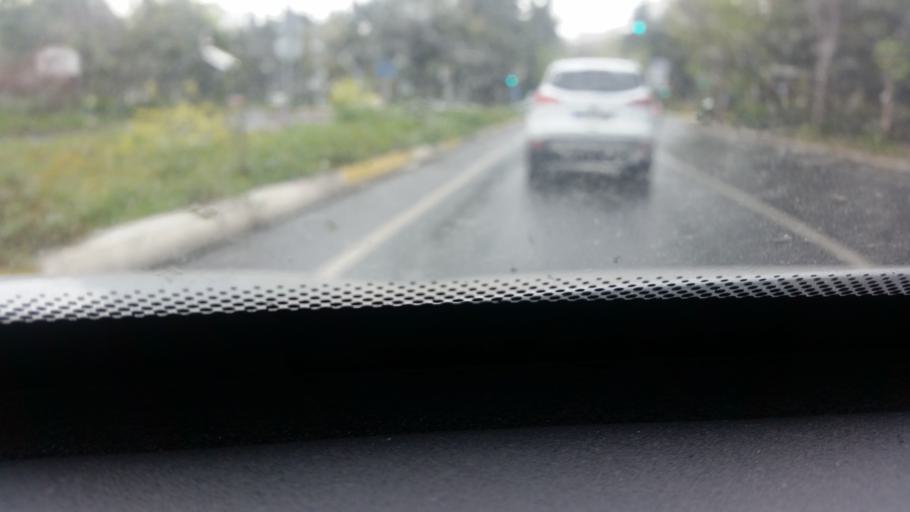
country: TR
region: Istanbul
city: Bahcelievler
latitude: 40.9827
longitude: 28.8532
